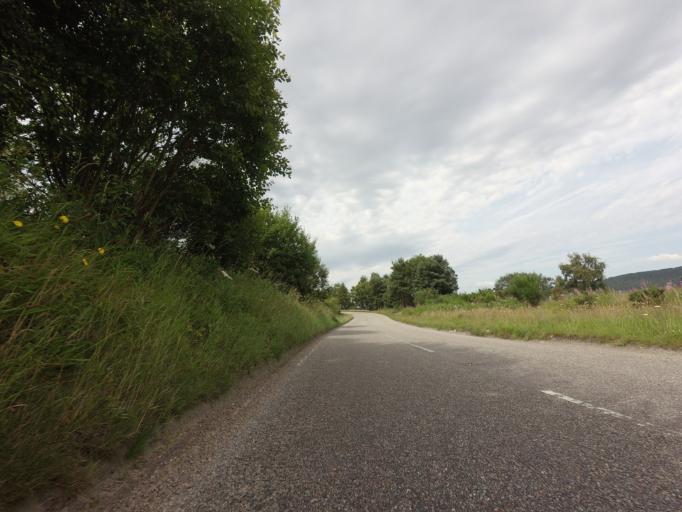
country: GB
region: Scotland
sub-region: Highland
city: Alness
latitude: 57.8611
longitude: -4.3168
